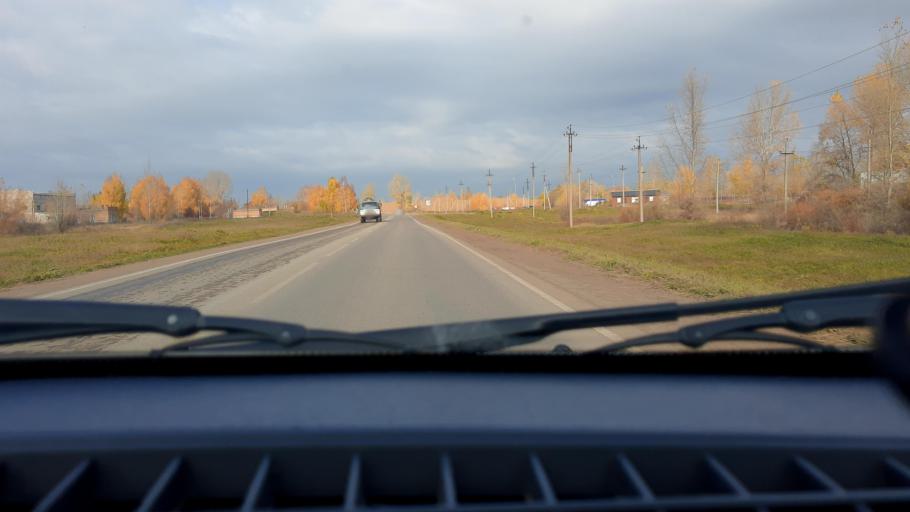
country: RU
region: Bashkortostan
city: Kabakovo
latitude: 54.5462
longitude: 56.1151
